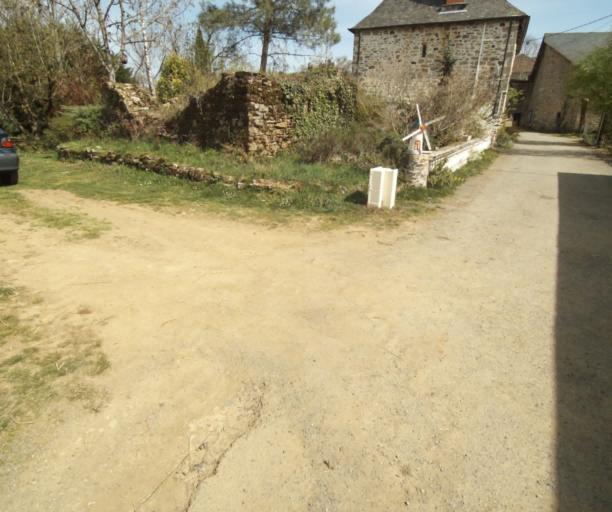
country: FR
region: Limousin
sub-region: Departement de la Correze
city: Naves
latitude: 45.3774
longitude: 1.7992
